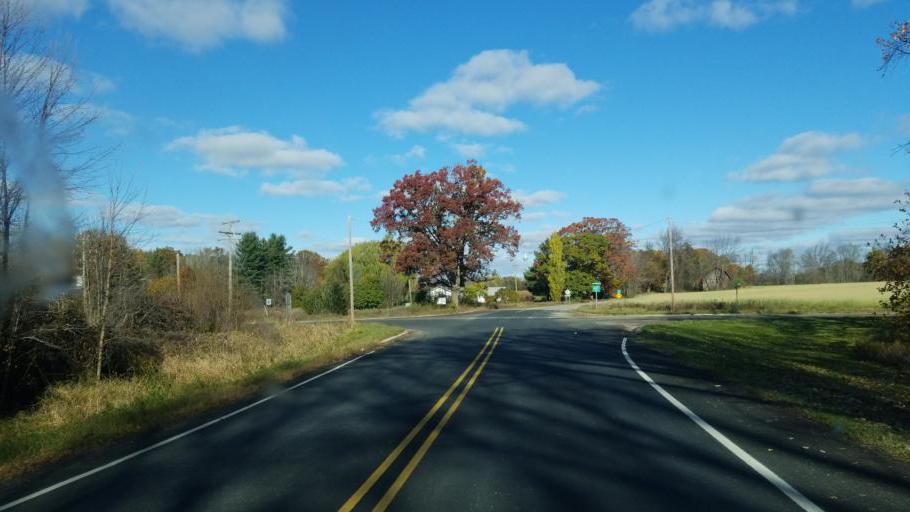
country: US
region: Michigan
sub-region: Montcalm County
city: Edmore
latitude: 43.4656
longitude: -85.0445
